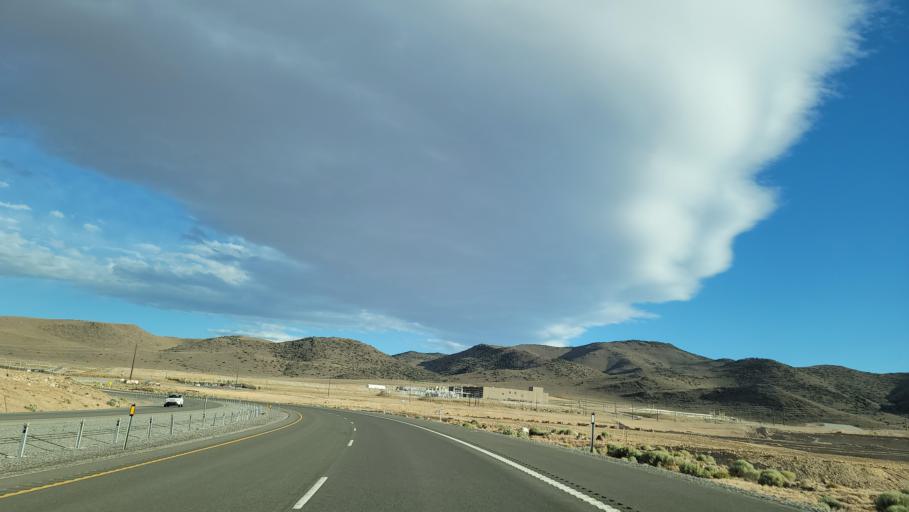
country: US
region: Nevada
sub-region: Lyon County
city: Stagecoach
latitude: 39.5063
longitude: -119.4338
